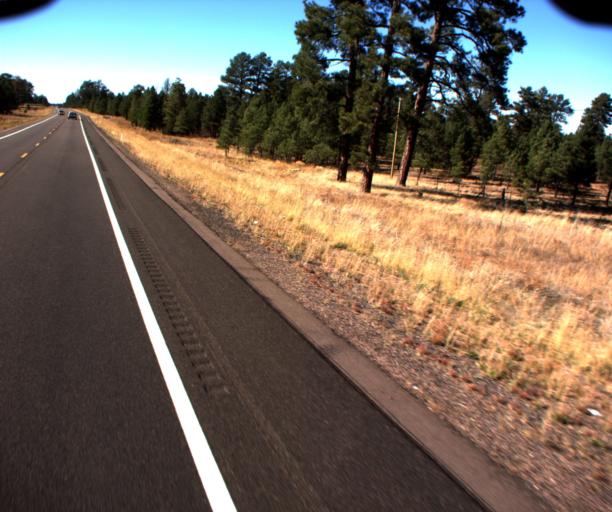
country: US
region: Arizona
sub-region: Apache County
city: Saint Michaels
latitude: 35.6966
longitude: -109.2764
